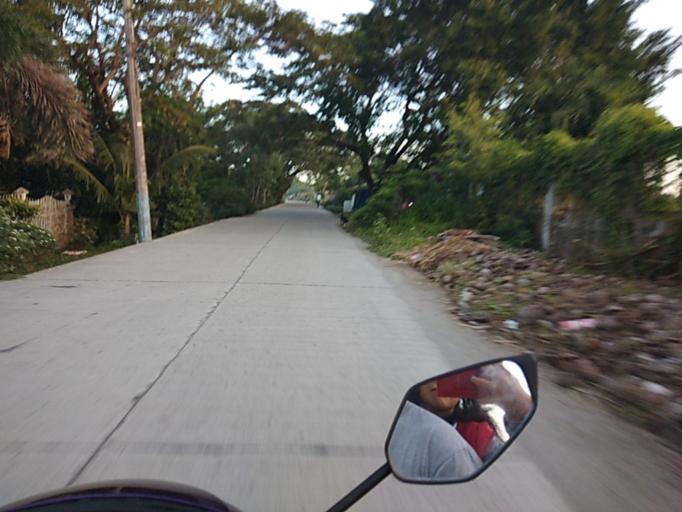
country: PH
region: Central Luzon
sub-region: Province of Bulacan
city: Balite
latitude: 14.8626
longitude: 120.7659
